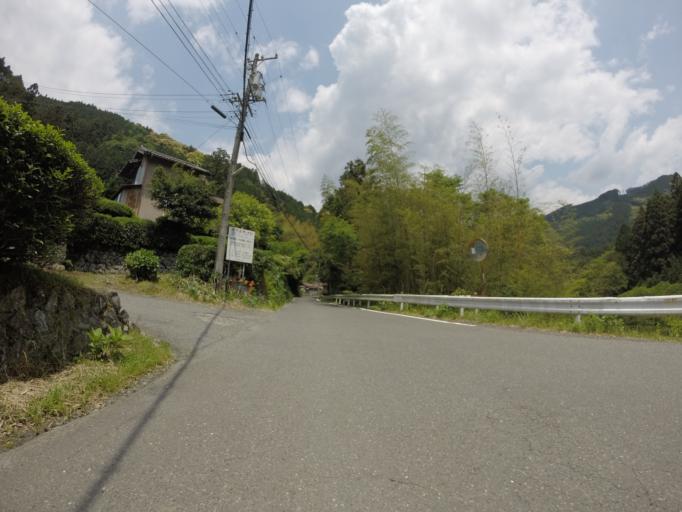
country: JP
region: Shizuoka
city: Shizuoka-shi
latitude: 35.1143
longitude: 138.3075
